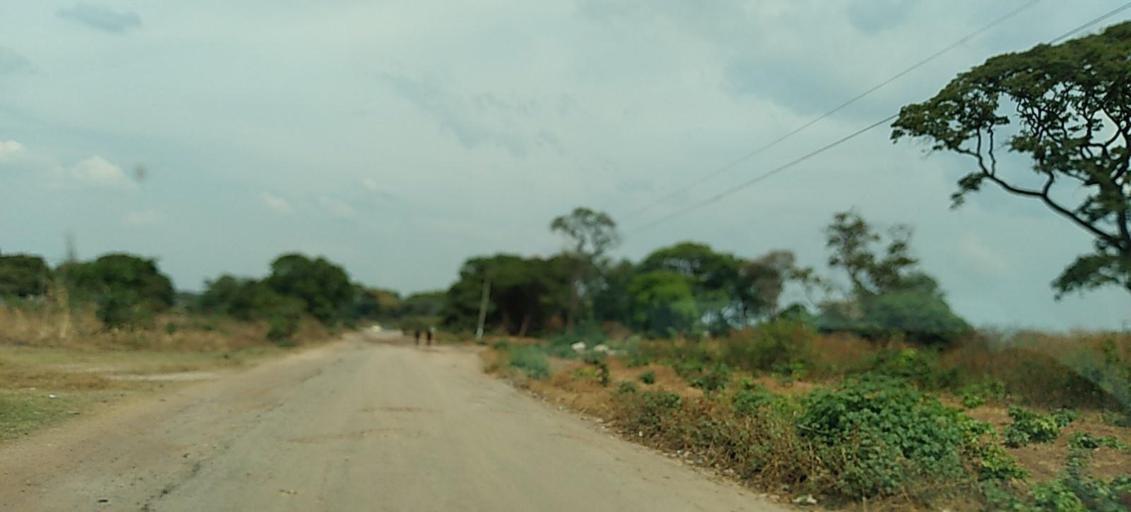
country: ZM
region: Copperbelt
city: Chililabombwe
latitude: -12.3733
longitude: 27.8250
